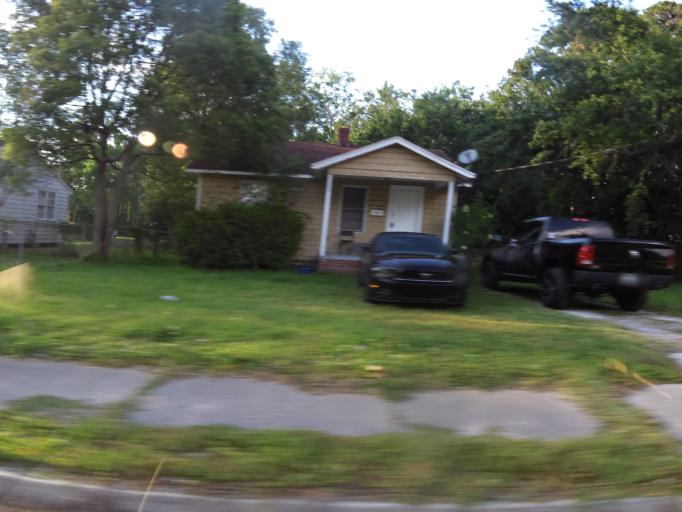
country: US
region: Florida
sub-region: Duval County
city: Jacksonville
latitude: 30.2920
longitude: -81.7332
